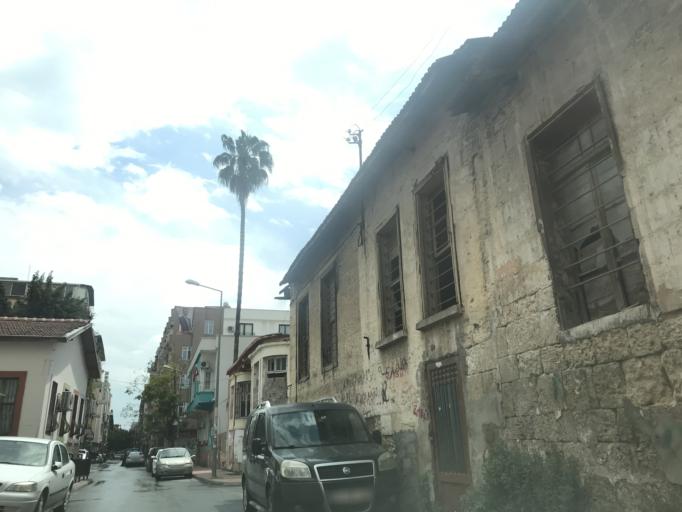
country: TR
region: Mersin
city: Mercin
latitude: 36.8023
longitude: 34.6292
